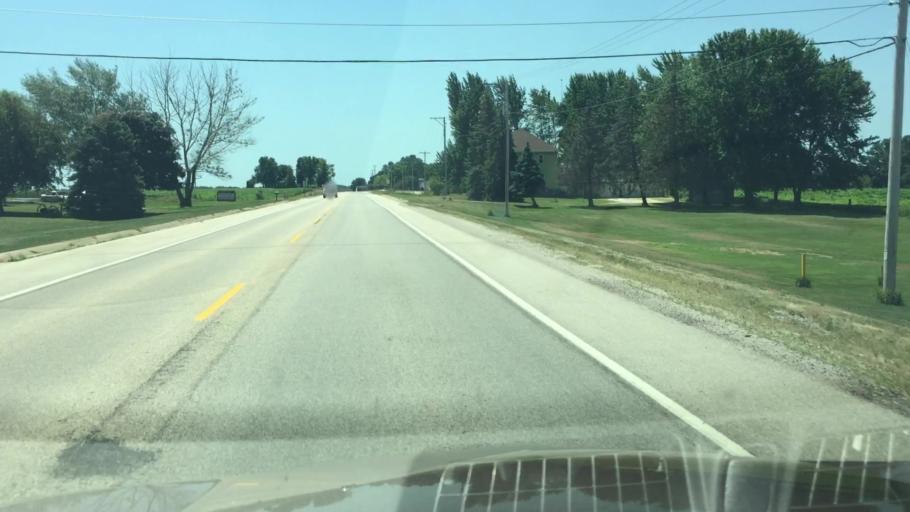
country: US
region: Wisconsin
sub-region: Fond du Lac County
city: Saint Peter
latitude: 43.9325
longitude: -88.3044
